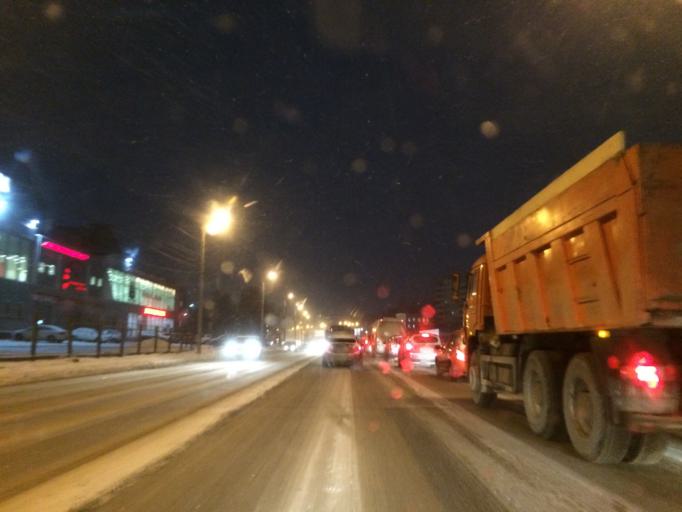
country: RU
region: Tula
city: Mendeleyevskiy
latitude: 54.1602
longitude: 37.6080
